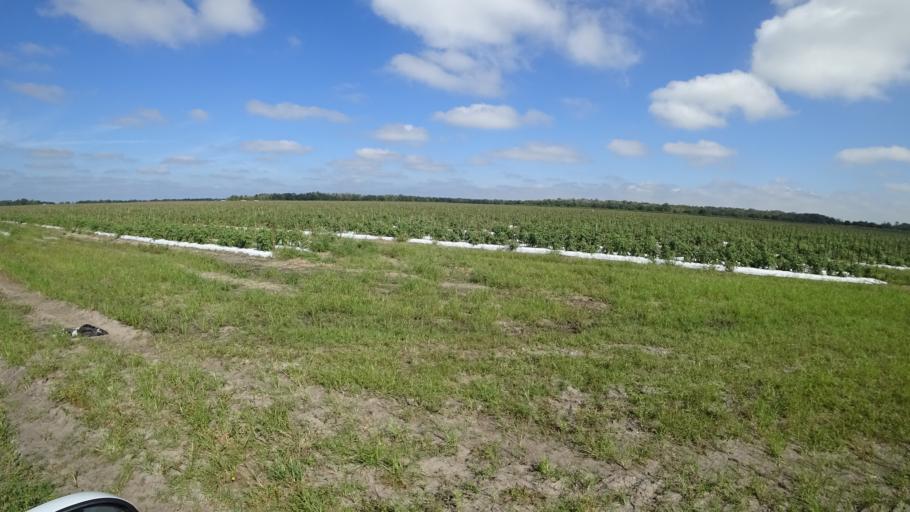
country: US
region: Florida
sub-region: DeSoto County
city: Arcadia
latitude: 27.2807
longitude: -82.0826
